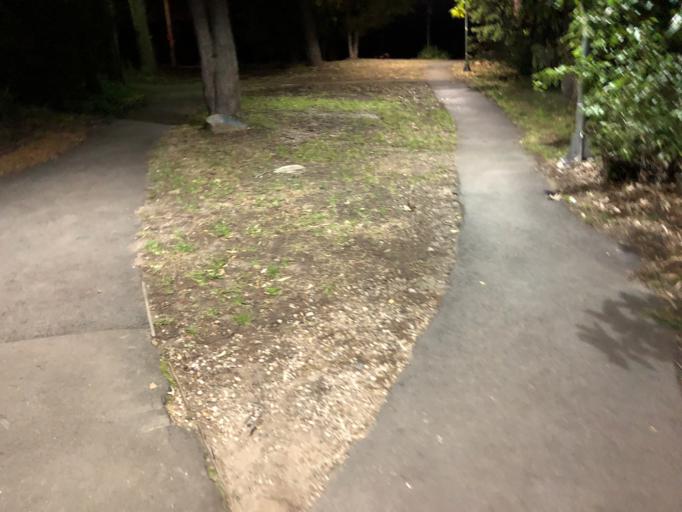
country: AU
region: New South Wales
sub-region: Hornsby Shire
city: Beecroft
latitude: -33.7490
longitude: 151.0670
